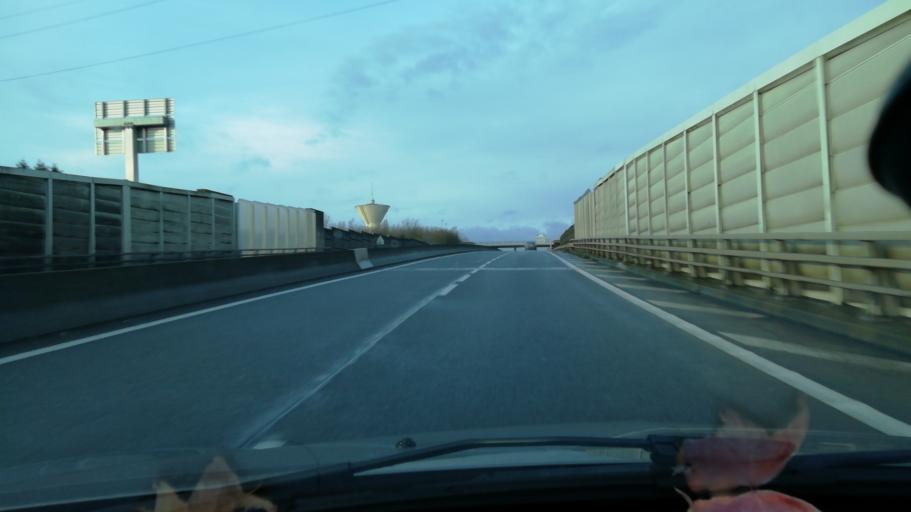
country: FR
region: Nord-Pas-de-Calais
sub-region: Departement du Nord
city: Hautmont
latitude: 50.2640
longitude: 3.9255
